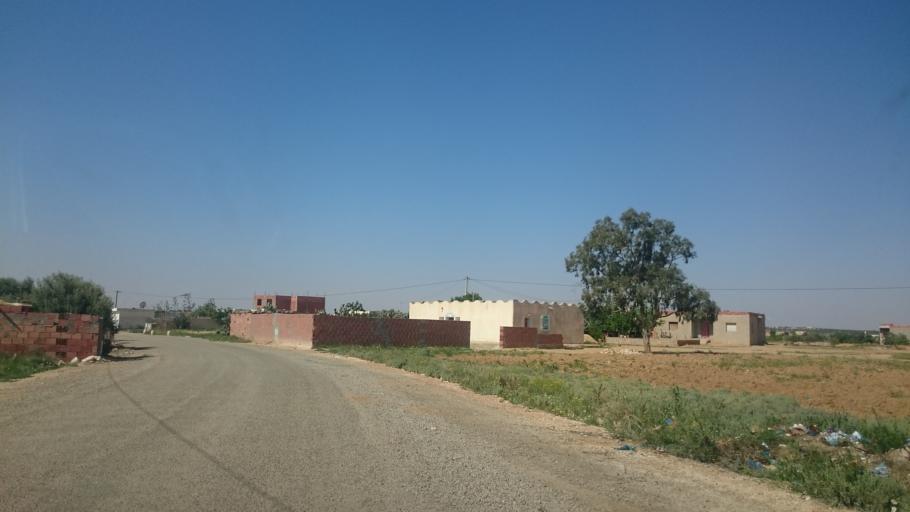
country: TN
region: Safaqis
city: Sfax
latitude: 34.7631
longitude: 10.5106
